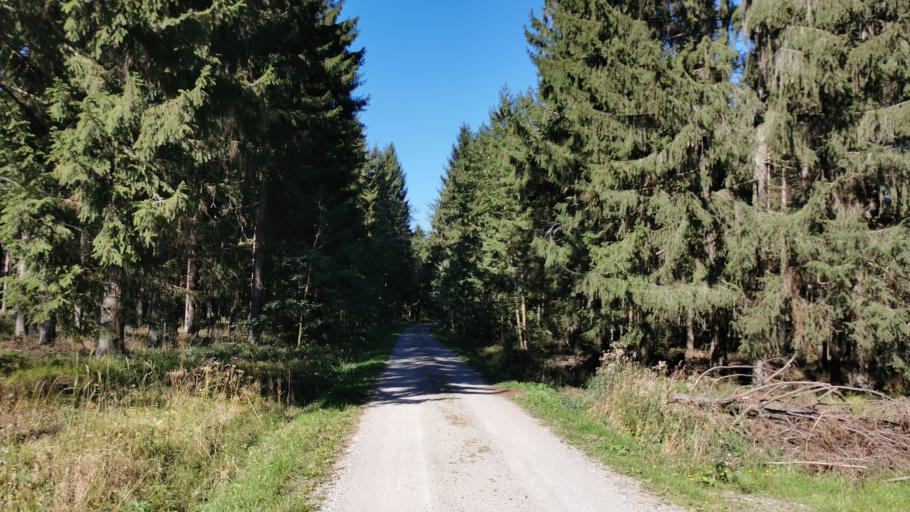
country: DE
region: Thuringia
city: Wurzbach
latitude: 50.4201
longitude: 11.5605
